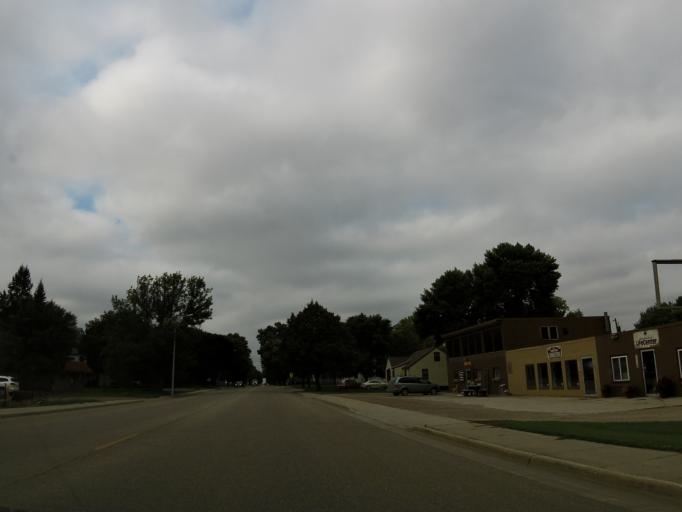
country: US
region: Minnesota
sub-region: Renville County
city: Renville
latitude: 44.7893
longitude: -95.2068
